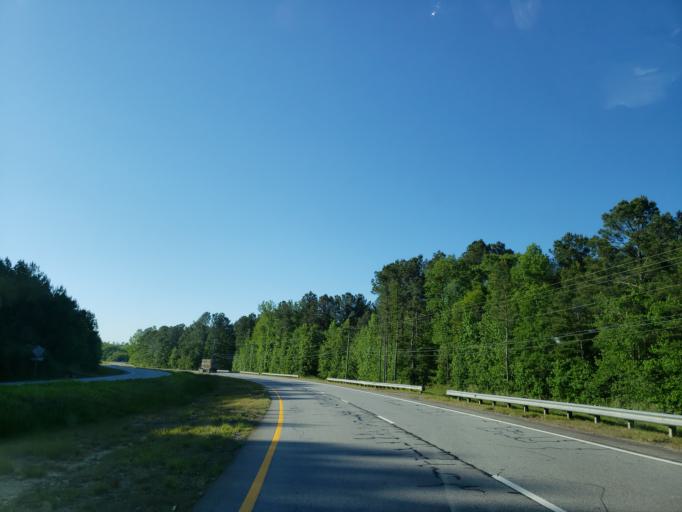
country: US
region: Georgia
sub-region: Haralson County
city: Buchanan
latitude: 33.8575
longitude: -85.2096
